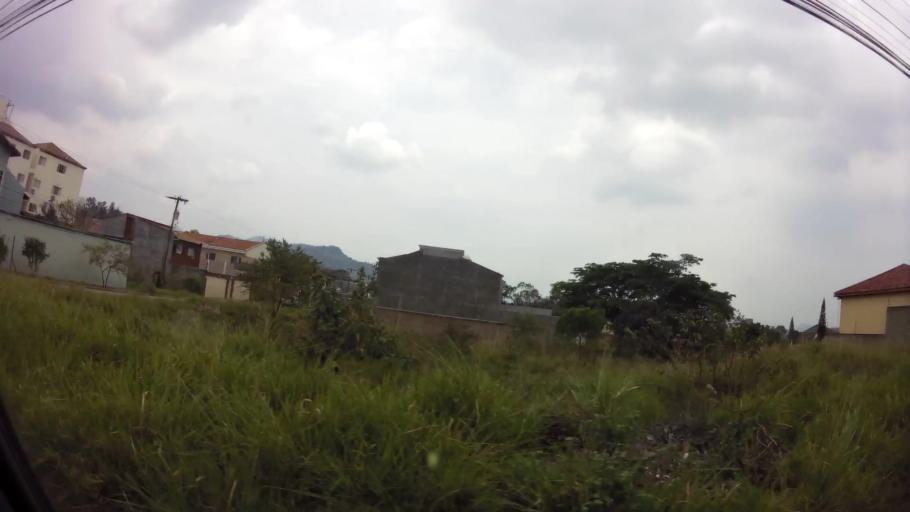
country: HN
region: Francisco Morazan
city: Tegucigalpa
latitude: 14.0762
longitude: -87.1776
